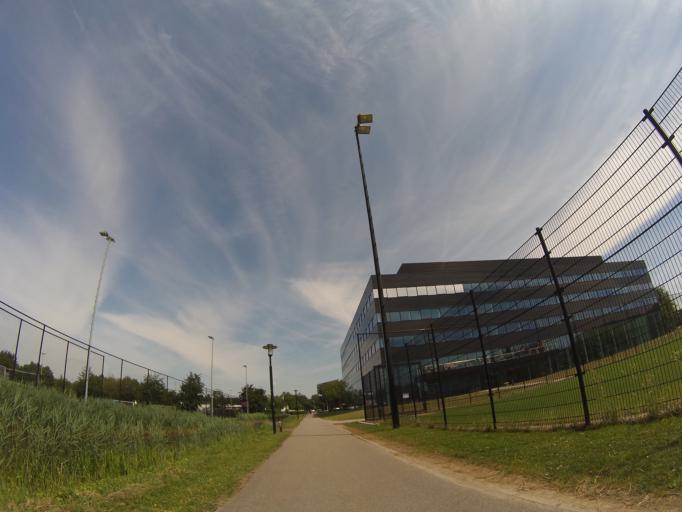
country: NL
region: Utrecht
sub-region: Gemeente De Bilt
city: De Bilt
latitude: 52.0890
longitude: 5.1745
